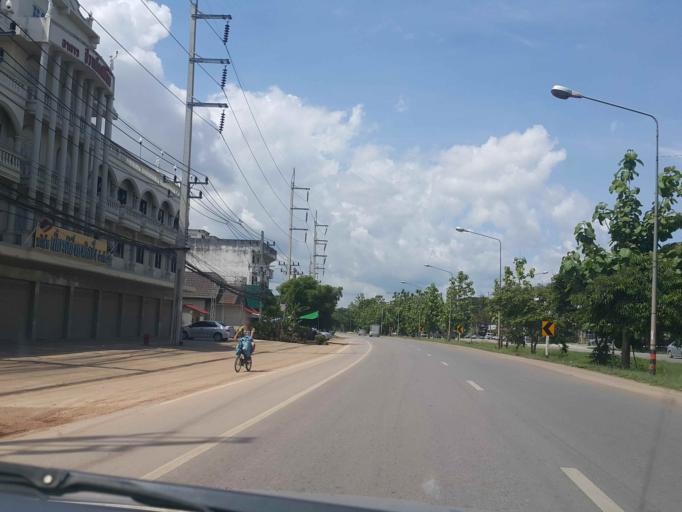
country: TH
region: Phayao
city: Phayao
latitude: 19.1549
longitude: 99.9135
